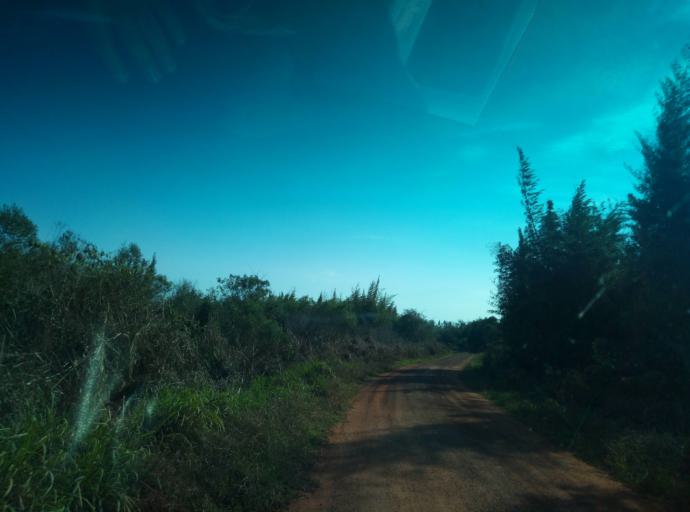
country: PY
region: Caaguazu
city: Doctor Cecilio Baez
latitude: -25.1648
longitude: -56.2228
